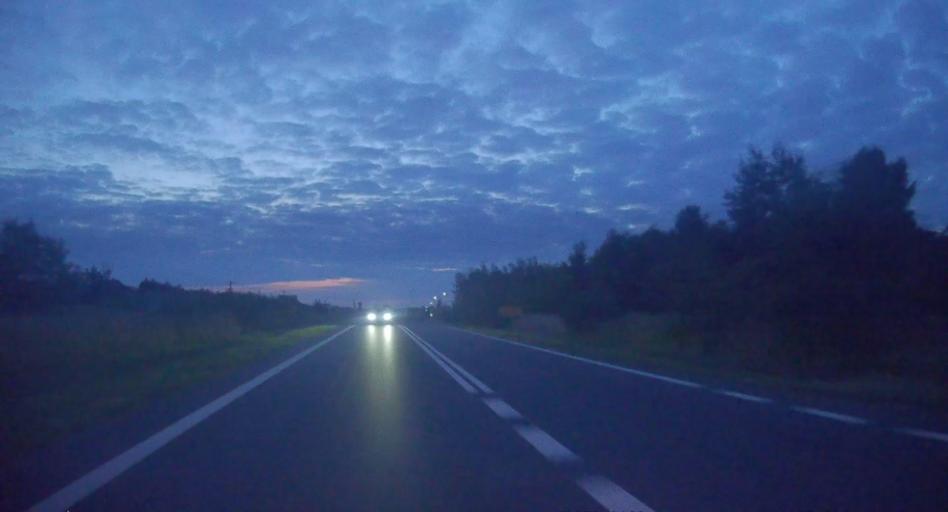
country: PL
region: Silesian Voivodeship
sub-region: Powiat klobucki
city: Kamyk
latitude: 50.8625
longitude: 19.0214
